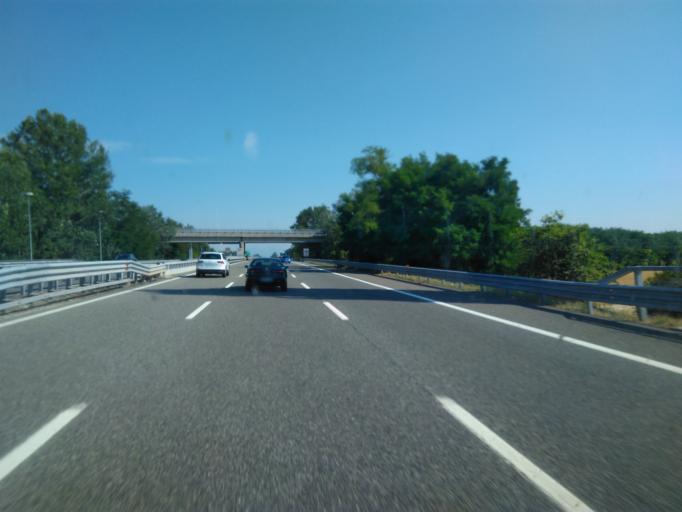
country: IT
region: Piedmont
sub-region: Provincia di Alessandria
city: Castellazzo Bormida
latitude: 44.8711
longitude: 8.5746
